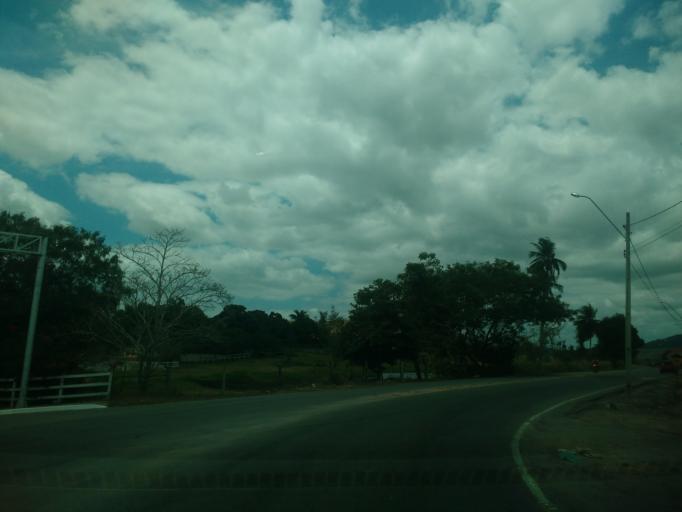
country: BR
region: Alagoas
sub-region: Uniao Dos Palmares
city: Uniao dos Palmares
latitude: -9.1557
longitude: -36.0361
